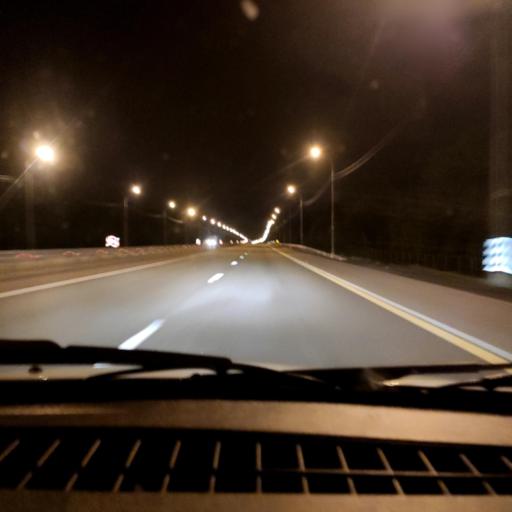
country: RU
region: Lipetsk
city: Zadonsk
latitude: 52.3478
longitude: 38.9516
